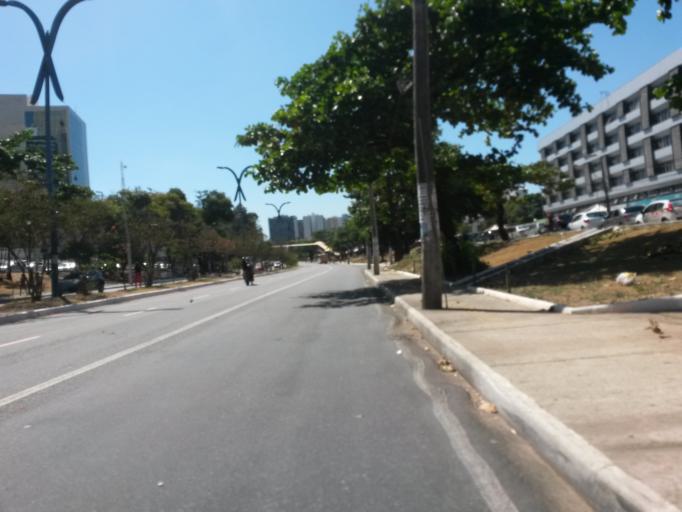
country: BR
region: Bahia
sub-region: Salvador
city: Salvador
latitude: -12.9968
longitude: -38.4650
